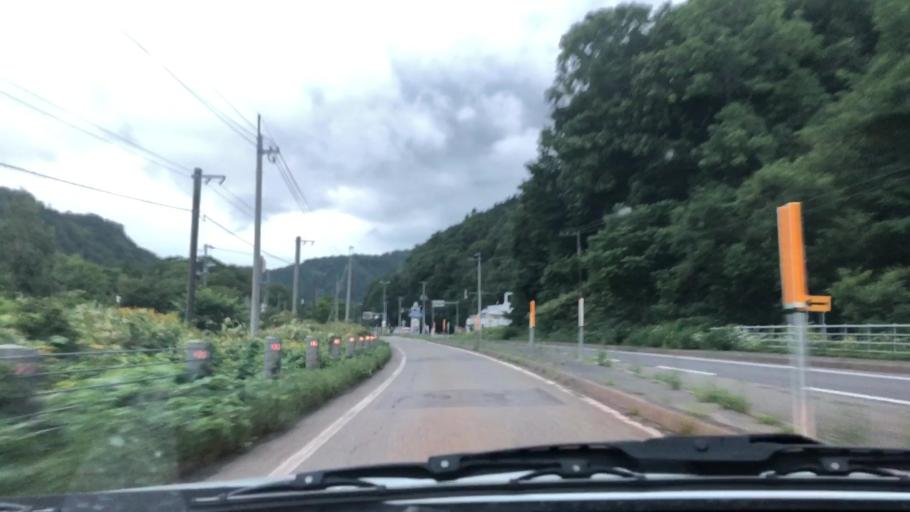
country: JP
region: Hokkaido
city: Chitose
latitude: 42.9126
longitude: 141.9713
